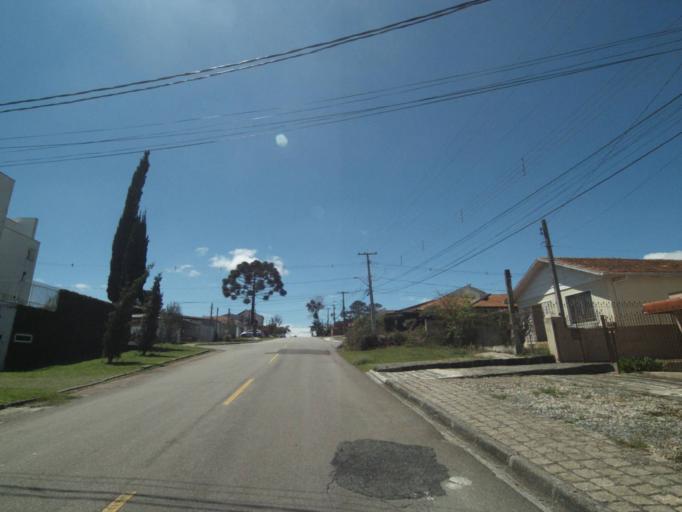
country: BR
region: Parana
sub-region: Curitiba
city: Curitiba
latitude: -25.3851
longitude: -49.2636
